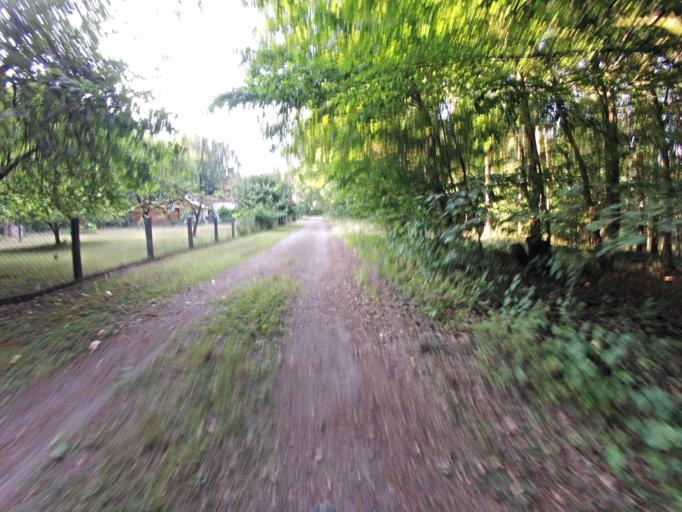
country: DE
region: North Rhine-Westphalia
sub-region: Regierungsbezirk Munster
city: Westerkappeln
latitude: 52.3148
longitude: 7.9036
